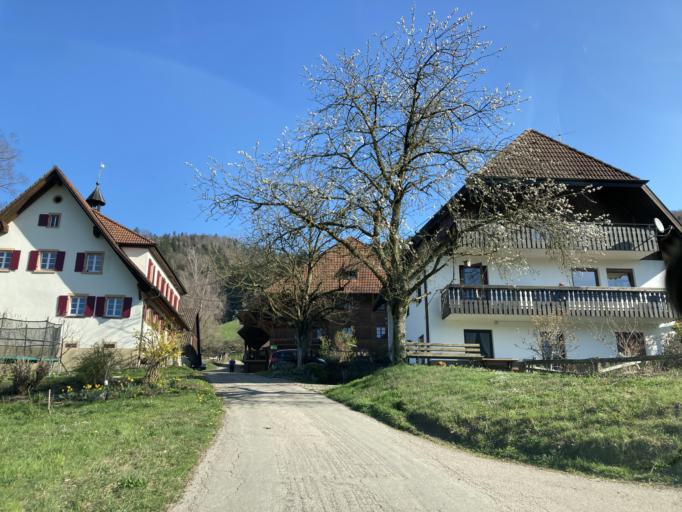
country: DE
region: Baden-Wuerttemberg
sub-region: Freiburg Region
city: Glottertal
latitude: 48.0503
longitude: 7.9723
